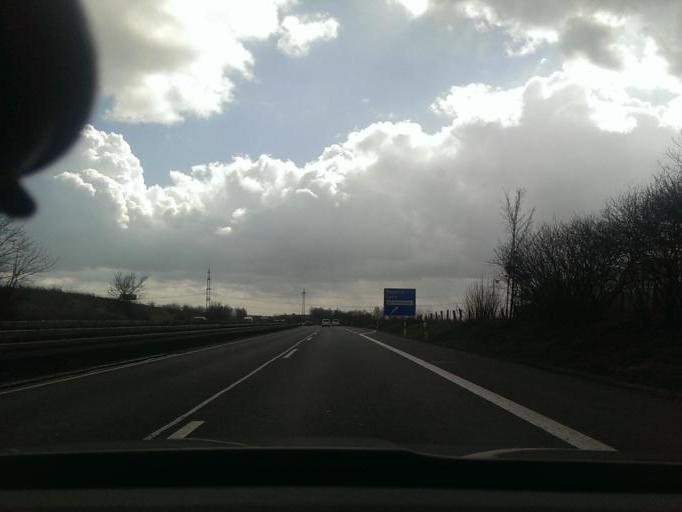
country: DE
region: Lower Saxony
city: Lehre
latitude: 52.3727
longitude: 10.7237
